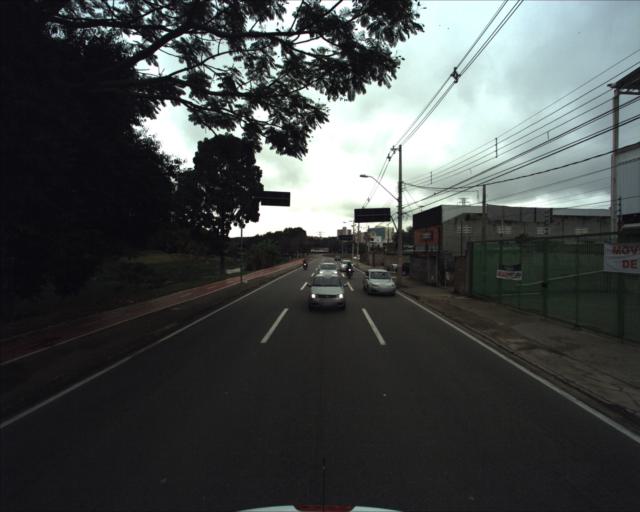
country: BR
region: Sao Paulo
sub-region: Sorocaba
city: Sorocaba
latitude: -23.5089
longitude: -47.4524
